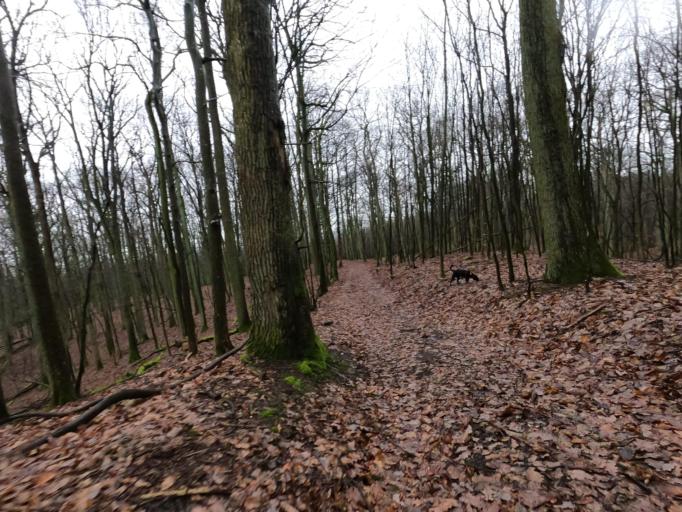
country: PL
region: Greater Poland Voivodeship
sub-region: Powiat pilski
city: Osiek nad Notecia
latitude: 53.1226
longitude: 17.2669
